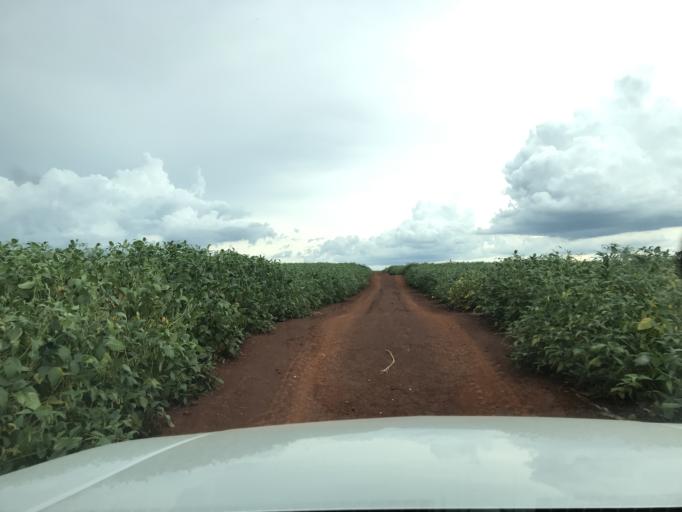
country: BR
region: Parana
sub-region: Palotina
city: Palotina
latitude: -24.2716
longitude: -53.7841
